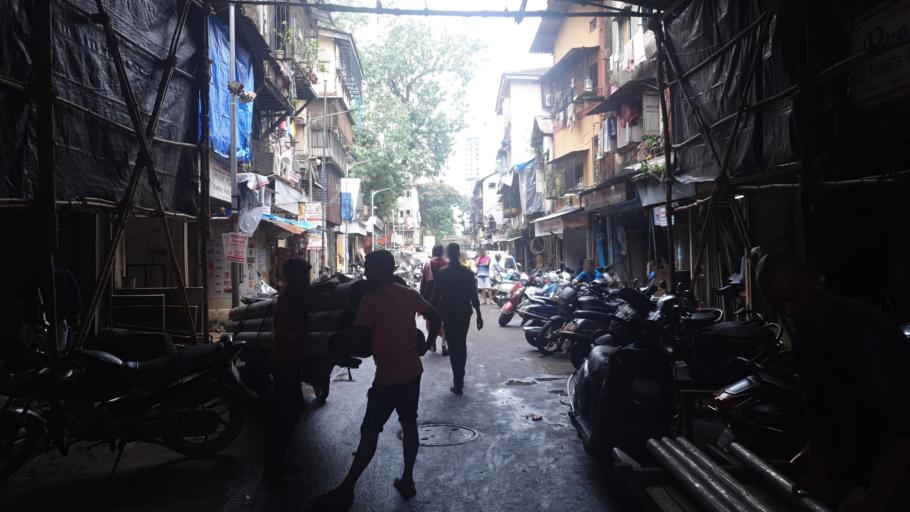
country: IN
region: Maharashtra
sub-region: Mumbai Suburban
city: Mumbai
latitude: 18.9594
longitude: 72.8272
